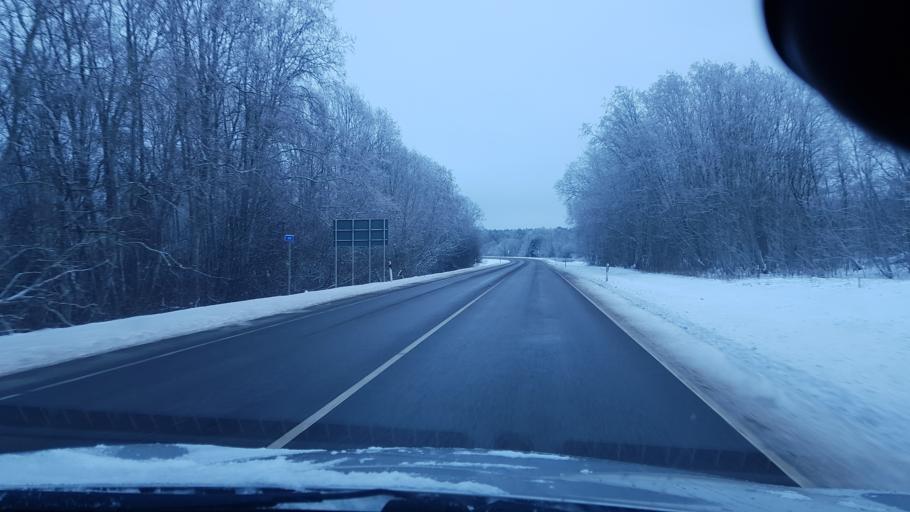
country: EE
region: Harju
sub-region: Paldiski linn
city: Paldiski
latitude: 59.3412
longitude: 24.1992
